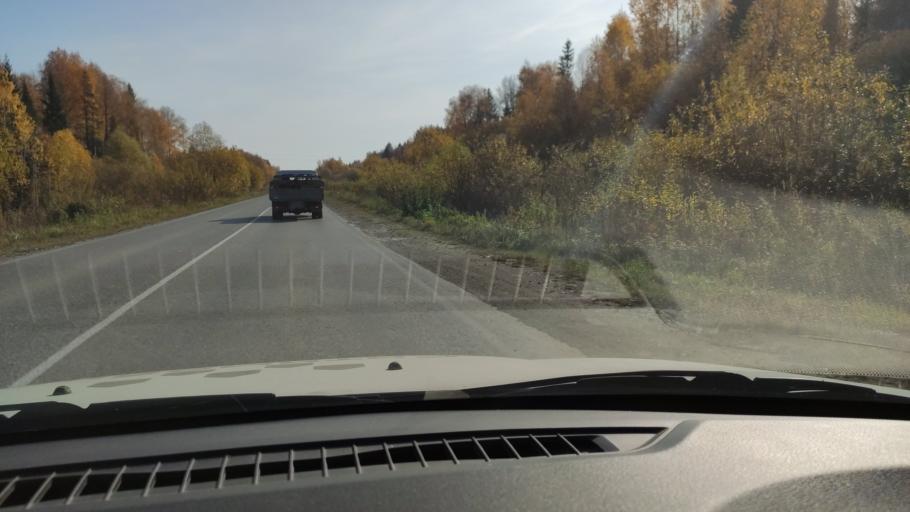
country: RU
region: Perm
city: Novyye Lyady
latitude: 58.0326
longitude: 56.6122
